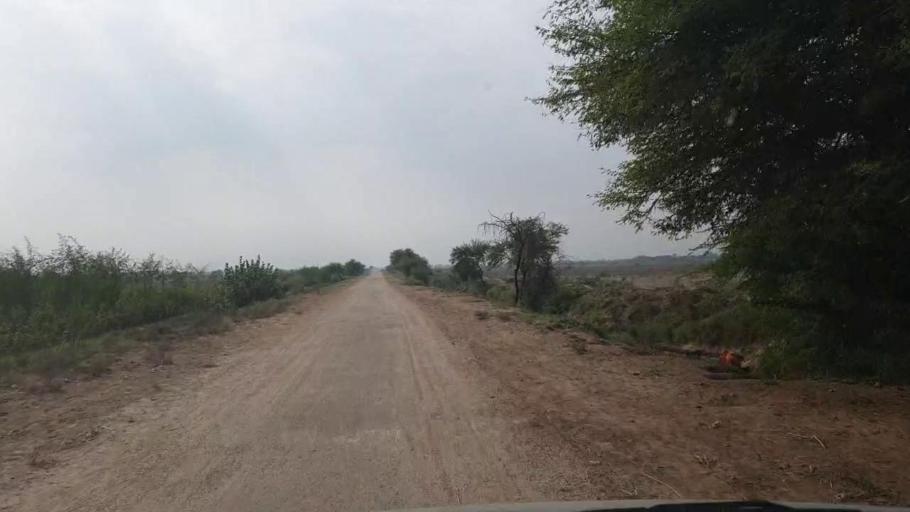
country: PK
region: Sindh
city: Talhar
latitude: 24.8730
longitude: 68.8381
